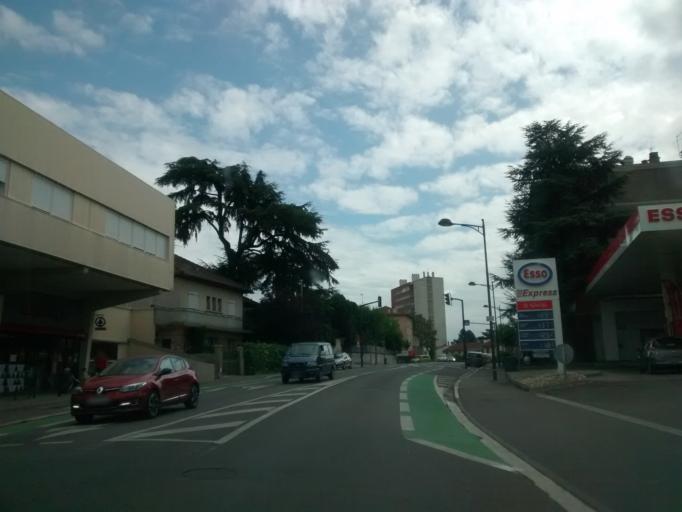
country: FR
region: Midi-Pyrenees
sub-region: Departement de la Haute-Garonne
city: Toulouse
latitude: 43.6264
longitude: 1.4590
